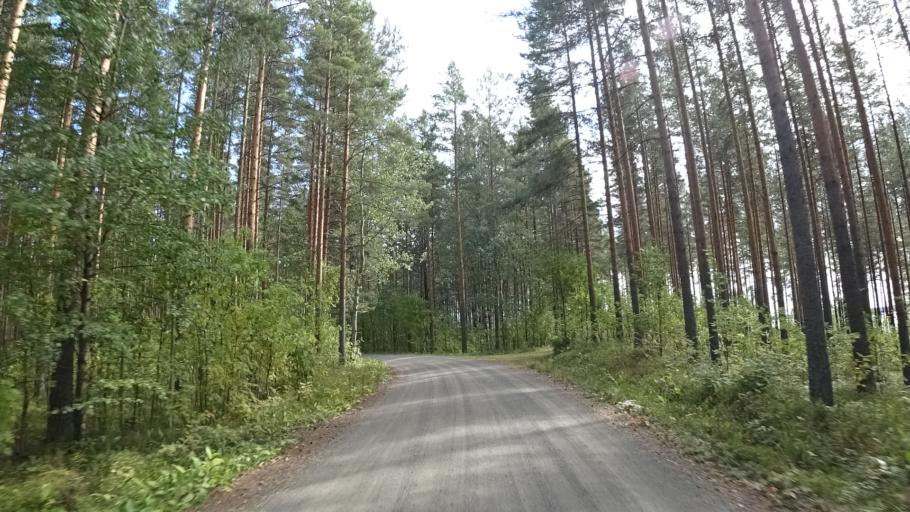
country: FI
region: North Karelia
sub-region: Keski-Karjala
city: Raeaekkylae
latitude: 62.3901
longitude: 29.7768
